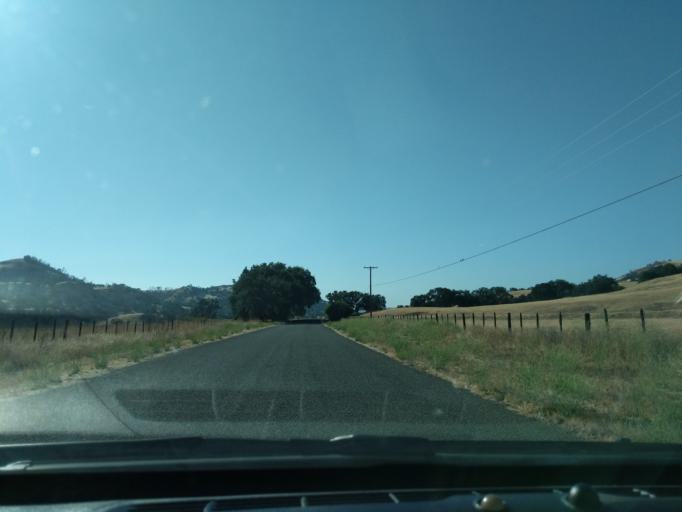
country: US
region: California
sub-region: San Luis Obispo County
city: San Miguel
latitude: 36.1159
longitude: -120.7268
